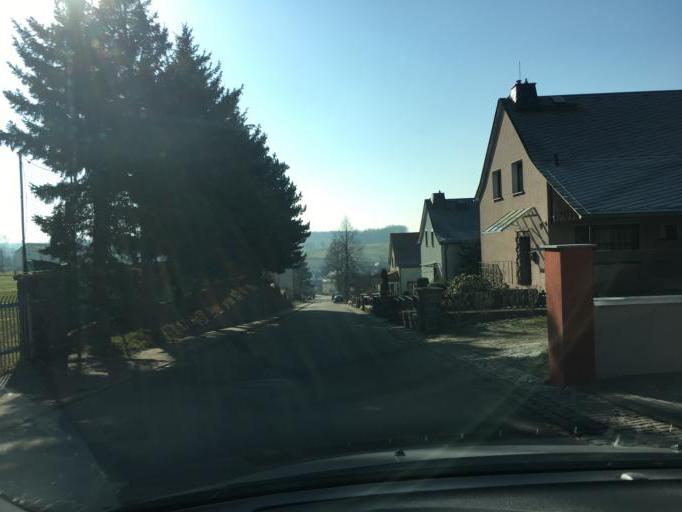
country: DE
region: Saxony
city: Lunzenau
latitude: 50.9650
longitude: 12.7490
